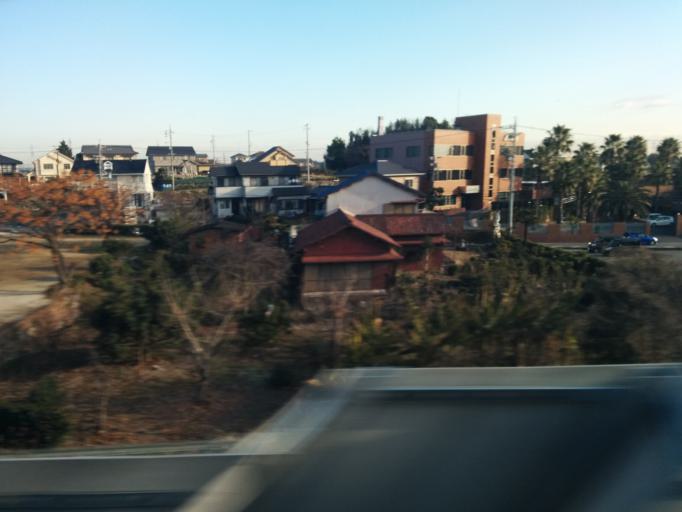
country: JP
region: Aichi
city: Obu
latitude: 35.0271
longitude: 136.9815
